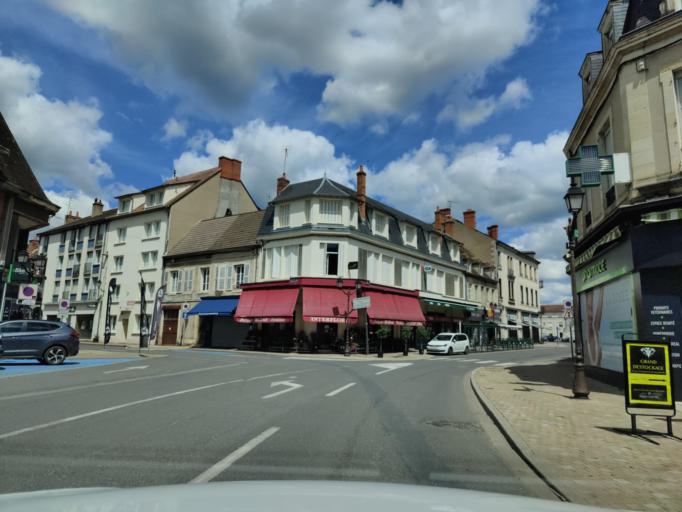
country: FR
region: Centre
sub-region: Departement du Cher
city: Saint-Amand-Montrond
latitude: 46.7215
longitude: 2.5044
